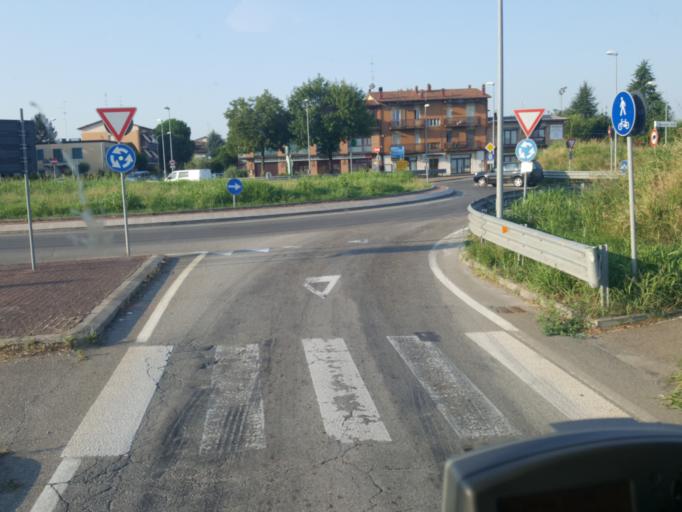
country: IT
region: Emilia-Romagna
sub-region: Provincia di Modena
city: Spilamberto
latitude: 44.5360
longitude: 11.0141
